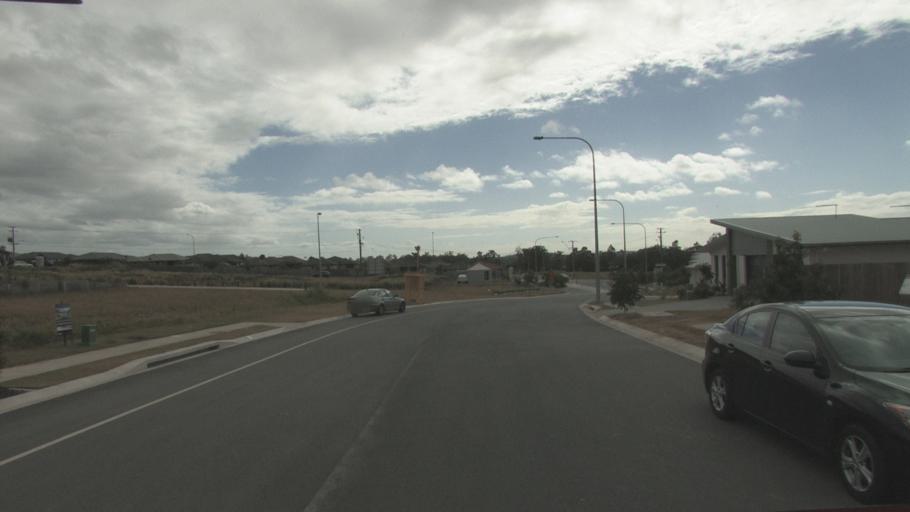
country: AU
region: Queensland
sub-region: Logan
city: Park Ridge South
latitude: -27.6905
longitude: 153.0485
